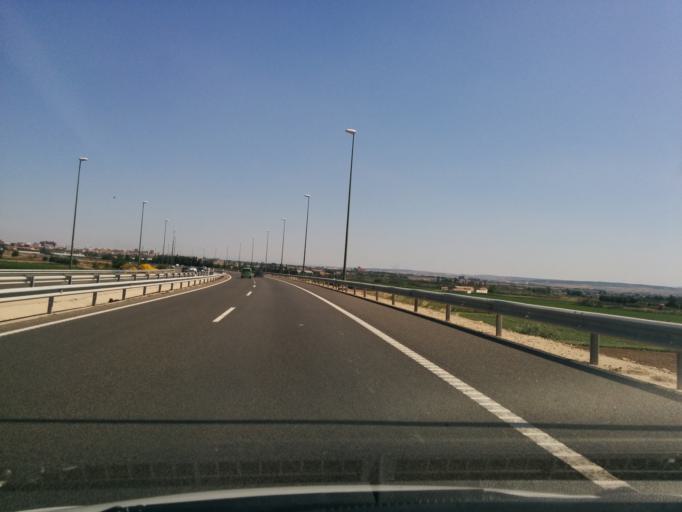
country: ES
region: Aragon
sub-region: Provincia de Zaragoza
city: Zaragoza
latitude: 41.6367
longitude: -0.8323
